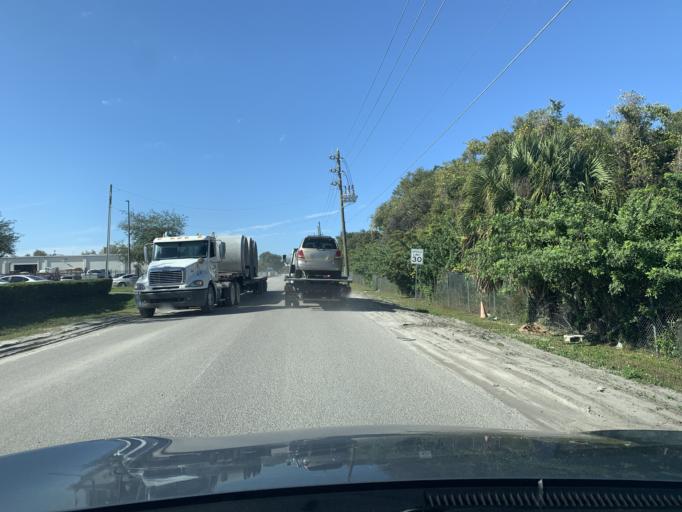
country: US
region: Florida
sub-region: Orange County
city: Lockhart
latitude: 28.6411
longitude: -81.4627
